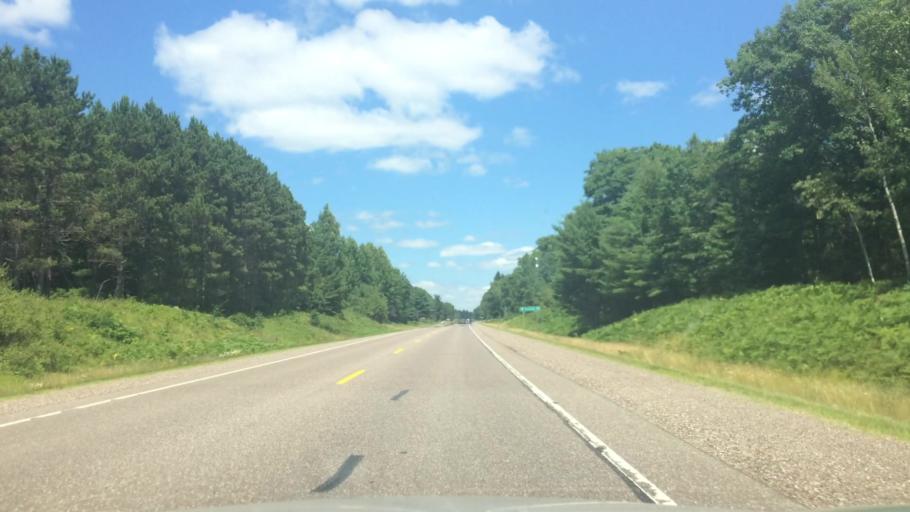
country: US
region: Wisconsin
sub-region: Vilas County
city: Lac du Flambeau
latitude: 45.9680
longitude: -89.6999
